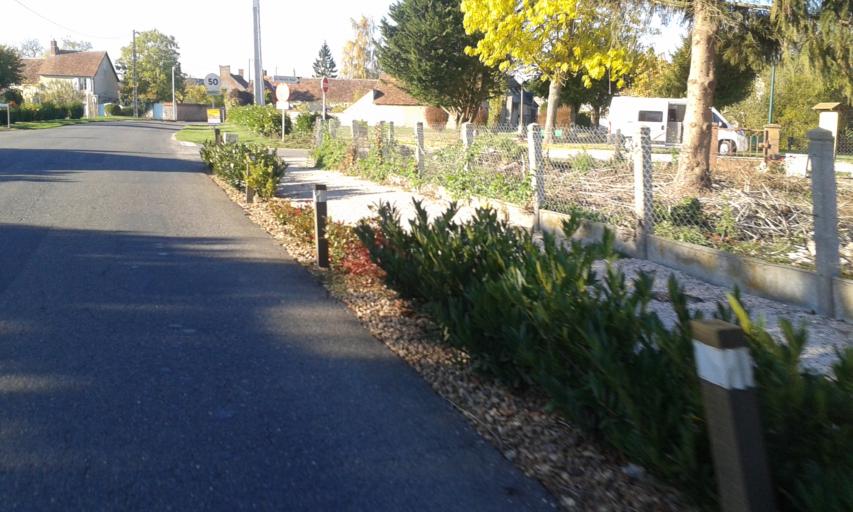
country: FR
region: Centre
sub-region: Departement du Loir-et-Cher
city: Oucques
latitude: 47.8295
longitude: 1.3835
